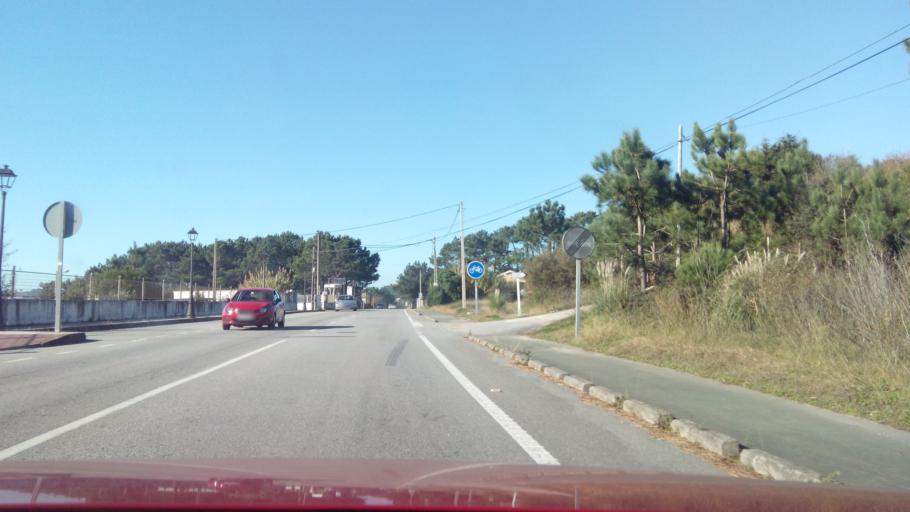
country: ES
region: Galicia
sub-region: Provincia de Pontevedra
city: O Grove
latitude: 42.4588
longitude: -8.8900
